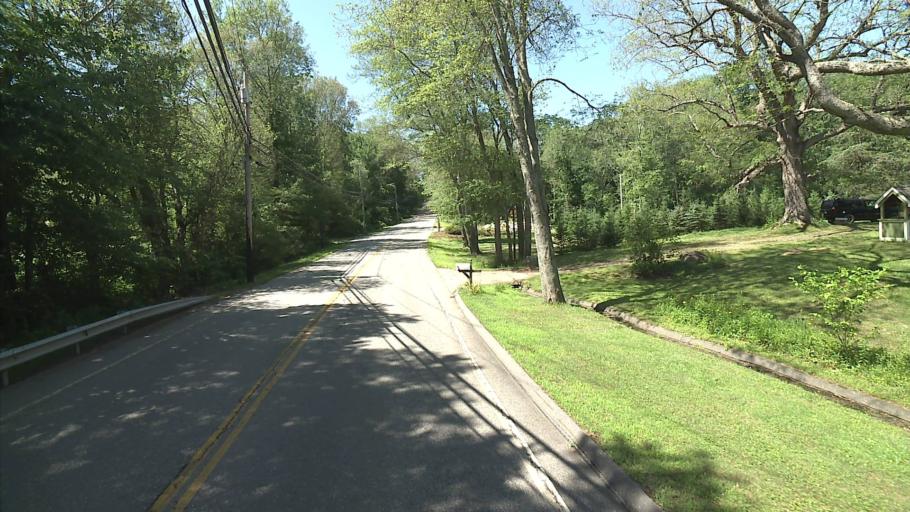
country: US
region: Connecticut
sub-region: New London County
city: Colchester
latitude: 41.5998
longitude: -72.2822
